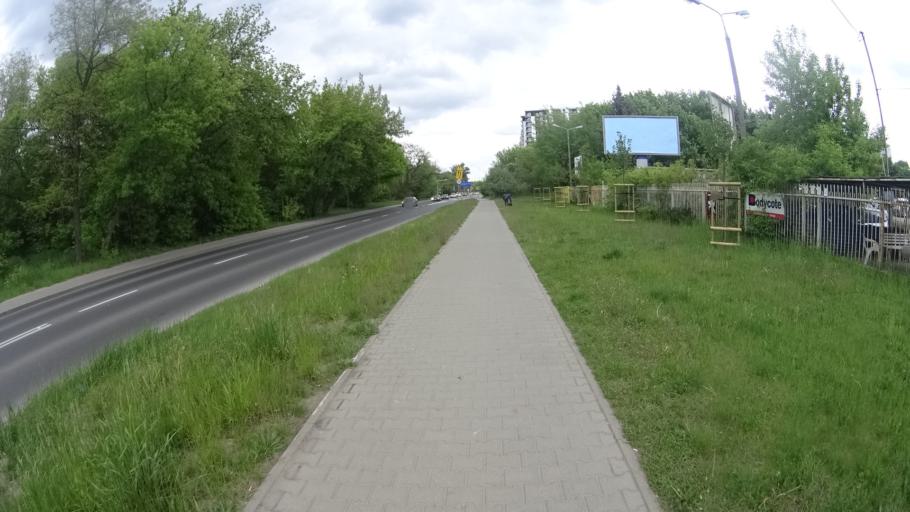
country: PL
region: Masovian Voivodeship
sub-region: Warszawa
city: Bielany
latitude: 52.2828
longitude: 20.9168
